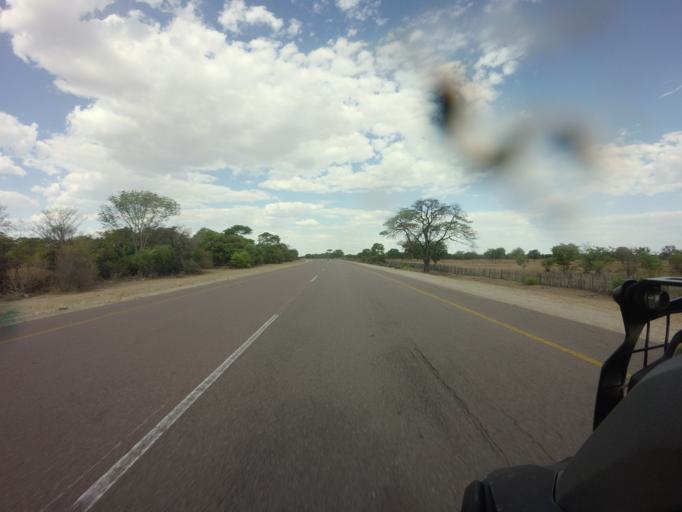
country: AO
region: Cunene
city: Ondjiva
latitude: -16.7150
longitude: 15.2794
